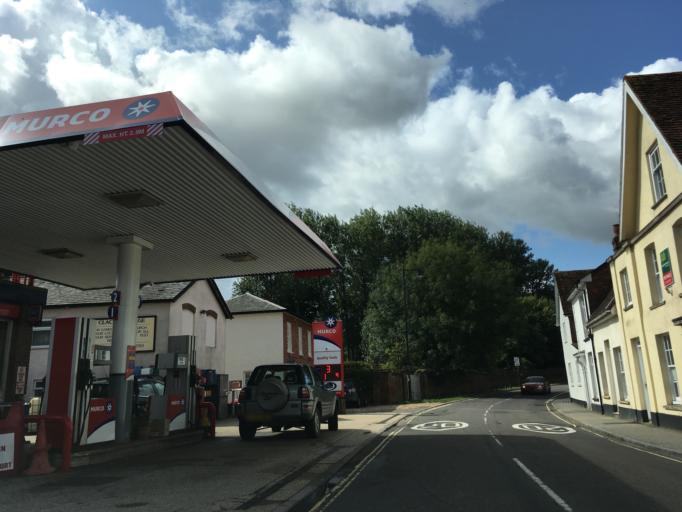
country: GB
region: England
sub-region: Hampshire
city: Overton
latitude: 51.2292
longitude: -1.3400
